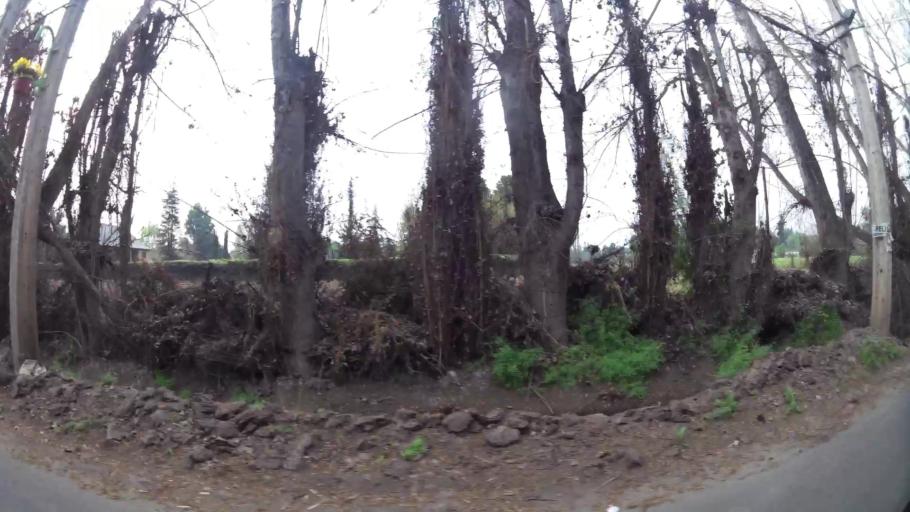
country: CL
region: Santiago Metropolitan
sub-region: Provincia de Chacabuco
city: Chicureo Abajo
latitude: -33.2685
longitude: -70.7084
